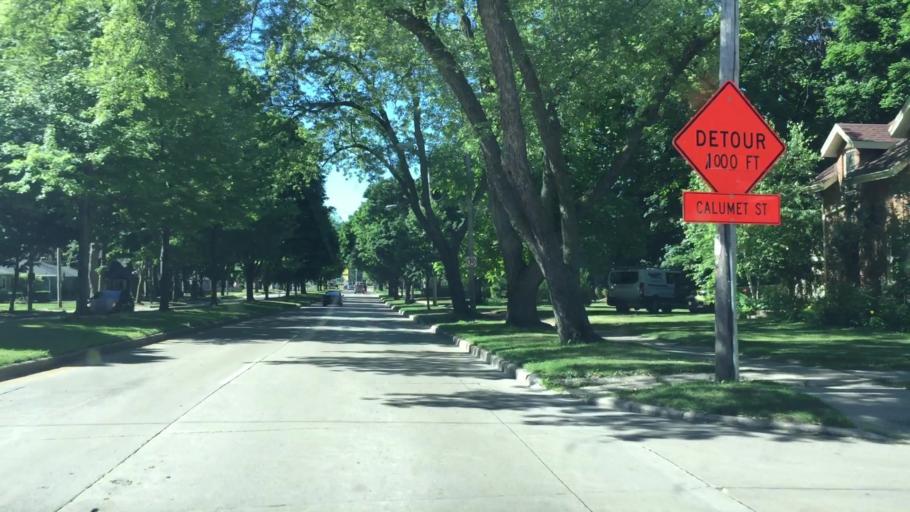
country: US
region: Wisconsin
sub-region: Outagamie County
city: Appleton
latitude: 44.2468
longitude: -88.4158
